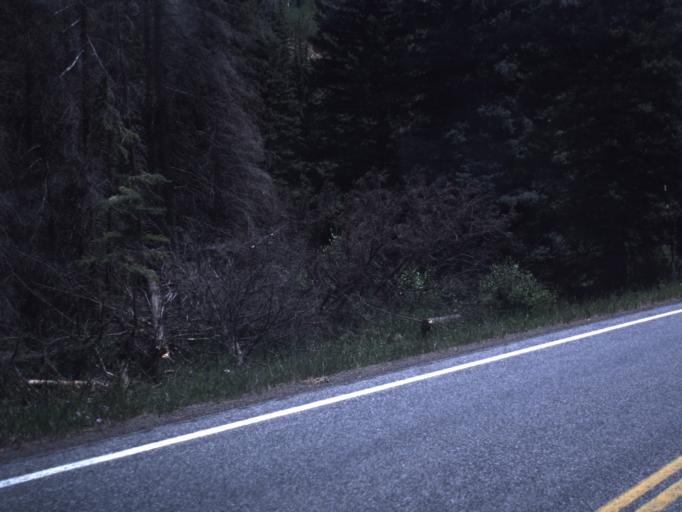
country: US
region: Utah
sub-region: Emery County
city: Huntington
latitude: 39.5281
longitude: -111.1543
